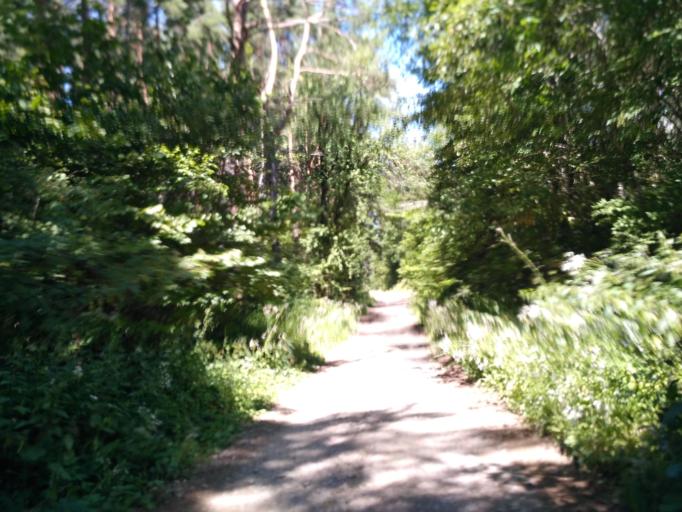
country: PL
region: Subcarpathian Voivodeship
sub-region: Powiat sanocki
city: Bukowsko
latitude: 49.4828
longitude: 22.0929
